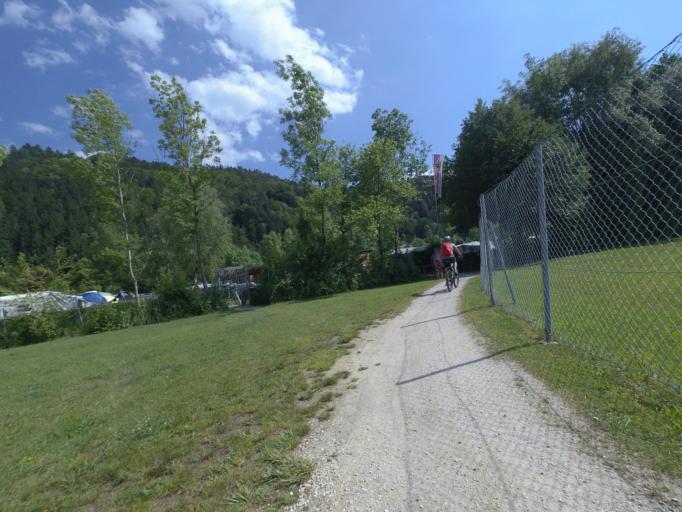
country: AT
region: Carinthia
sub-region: Politischer Bezirk Villach Land
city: Ferndorf
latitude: 46.7691
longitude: 13.6476
